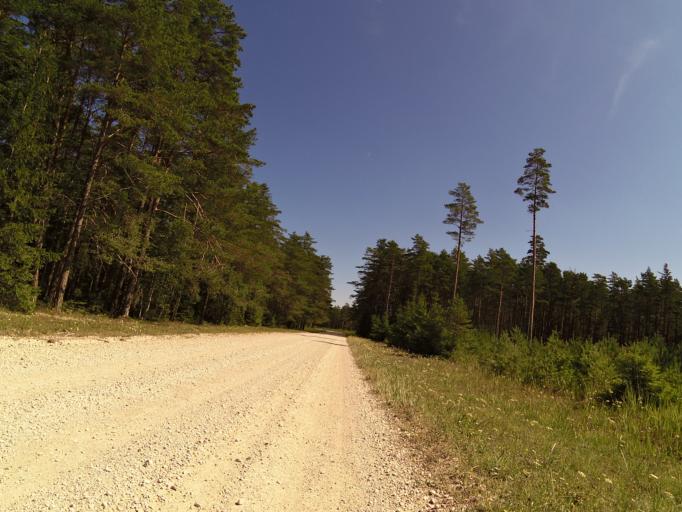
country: EE
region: Hiiumaa
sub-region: Kaerdla linn
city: Kardla
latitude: 58.9147
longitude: 22.3361
